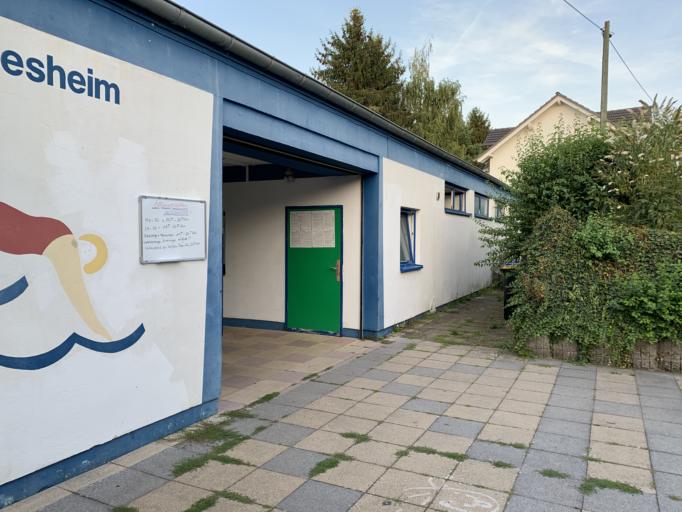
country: DE
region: Rheinland-Pfalz
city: Windesheim
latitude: 49.9073
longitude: 7.8102
